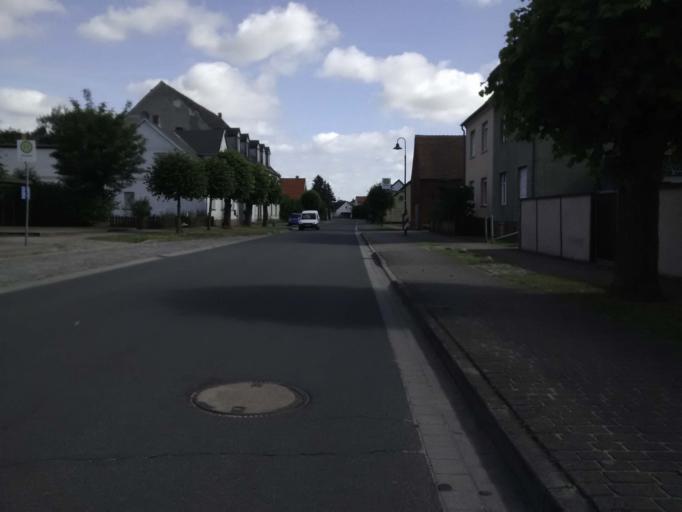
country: DE
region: Saxony-Anhalt
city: Jerichow
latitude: 52.4144
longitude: 11.9643
